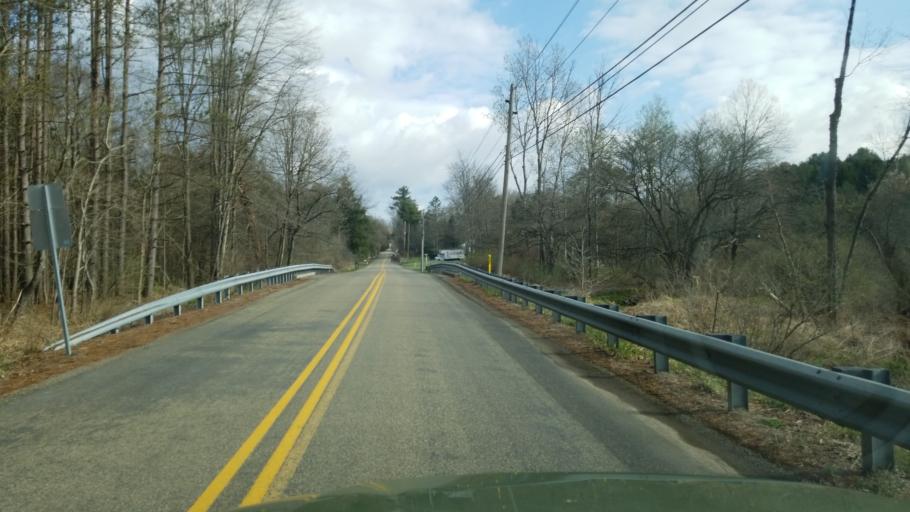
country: US
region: Pennsylvania
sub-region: Jefferson County
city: Brockway
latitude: 41.2510
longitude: -78.8383
